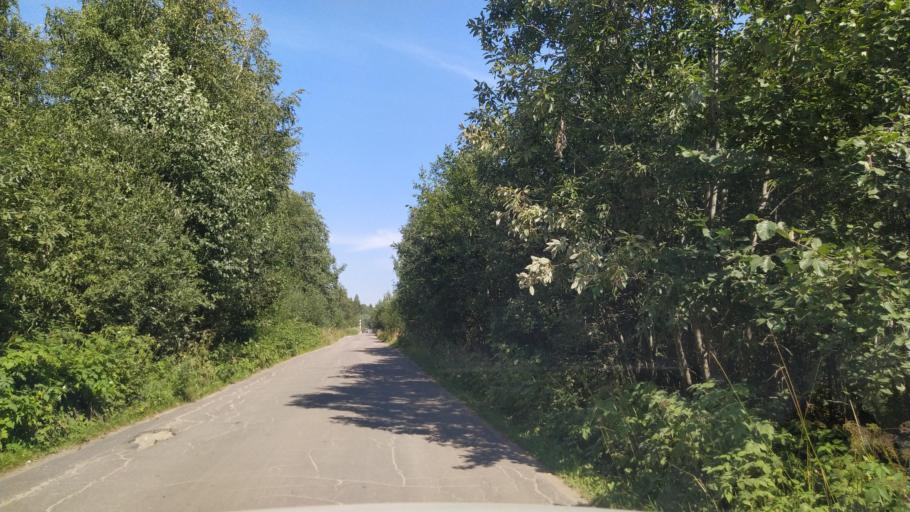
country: RU
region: Leningrad
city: Siverskiy
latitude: 59.2848
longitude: 30.0298
